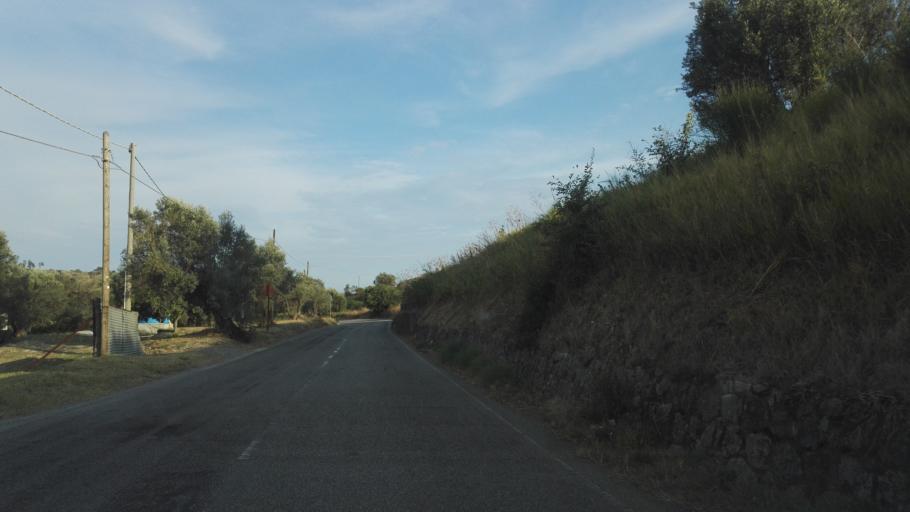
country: IT
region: Calabria
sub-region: Provincia di Reggio Calabria
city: Stignano
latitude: 38.3811
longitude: 16.4782
